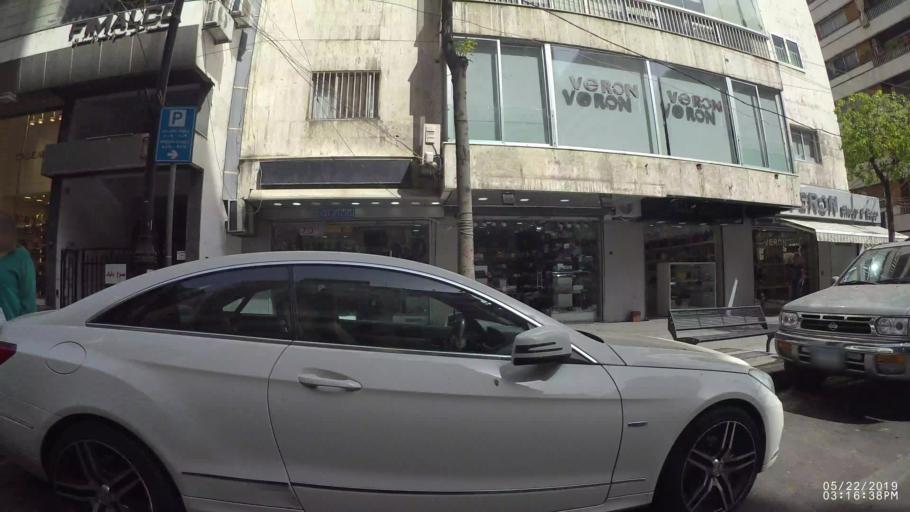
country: LB
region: Beyrouth
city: Beirut
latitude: 33.8831
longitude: 35.4916
